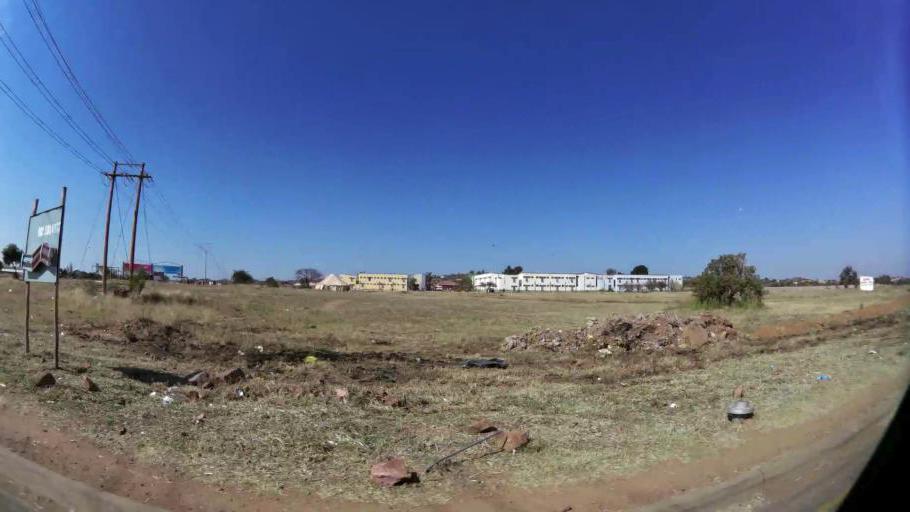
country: ZA
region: Gauteng
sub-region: City of Tshwane Metropolitan Municipality
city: Mabopane
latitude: -25.5215
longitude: 28.0890
